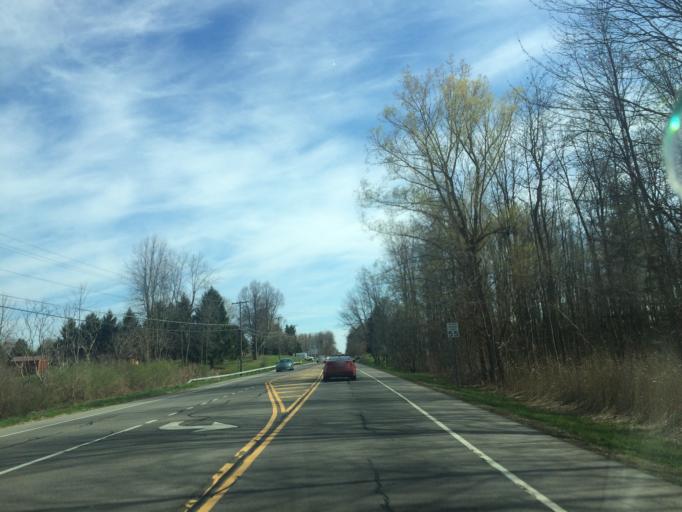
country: US
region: New York
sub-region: Monroe County
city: Webster
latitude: 43.1811
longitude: -77.4308
